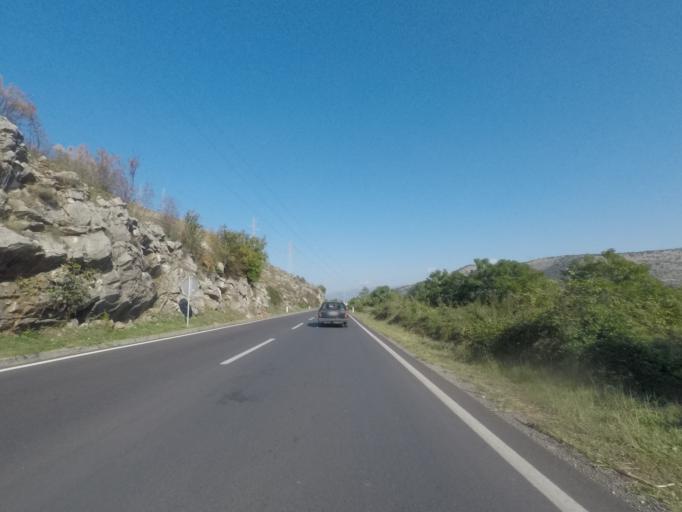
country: ME
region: Podgorica
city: Podgorica
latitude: 42.4458
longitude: 19.2026
